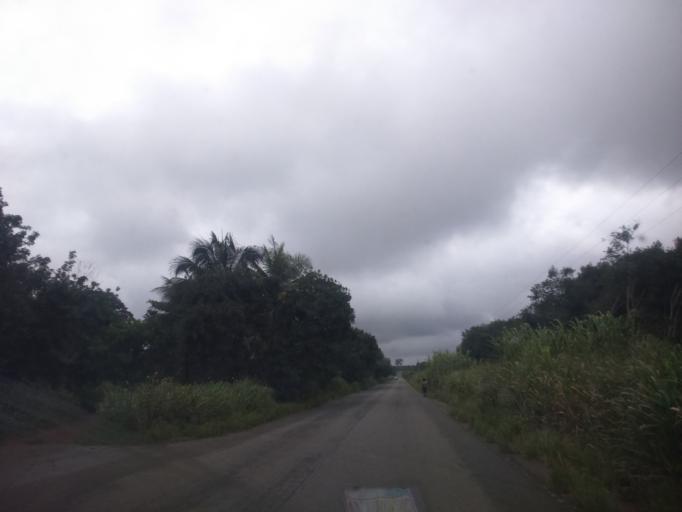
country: CI
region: Sud-Comoe
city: Adiake
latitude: 5.2920
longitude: -3.4494
